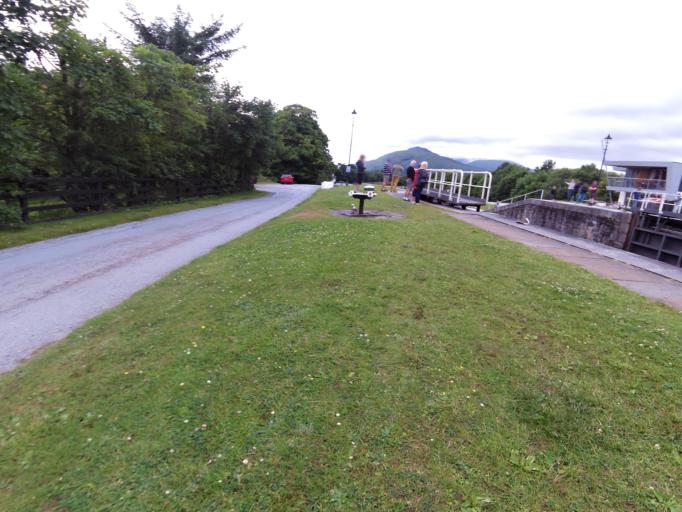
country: GB
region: Scotland
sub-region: Highland
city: Fort William
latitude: 56.8459
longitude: -5.0943
